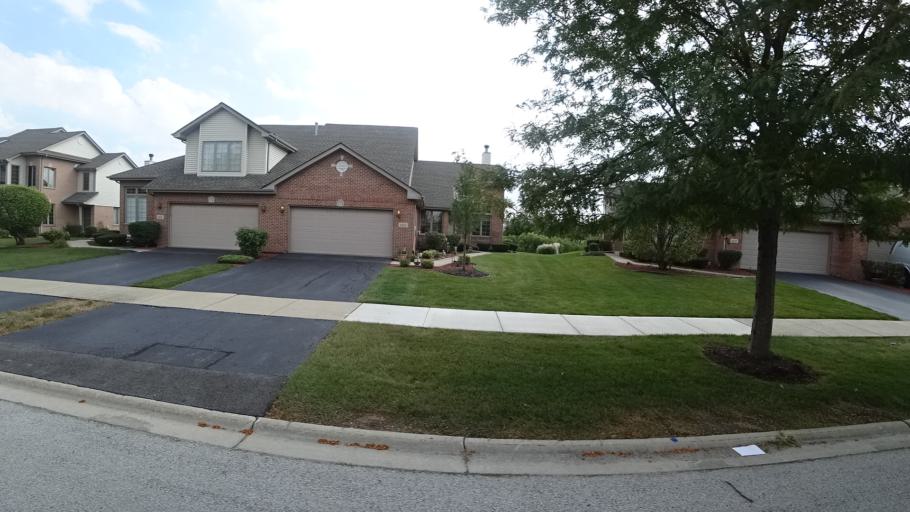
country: US
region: Illinois
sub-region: Cook County
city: Tinley Park
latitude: 41.5556
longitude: -87.7794
